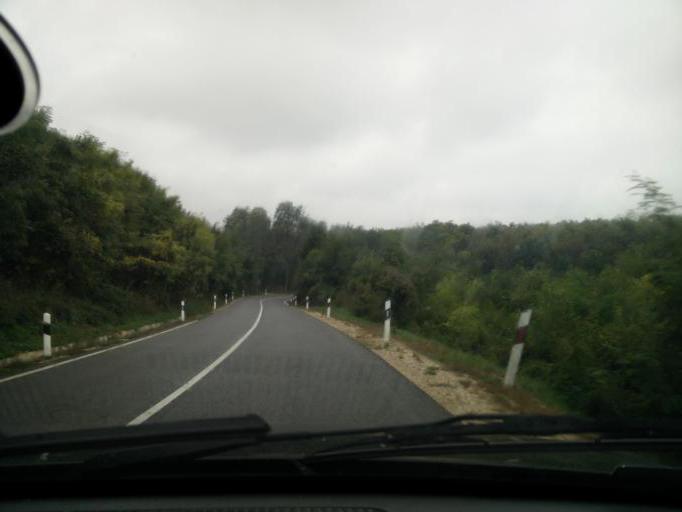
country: HU
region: Komarom-Esztergom
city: Bajna
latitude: 47.6367
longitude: 18.5606
